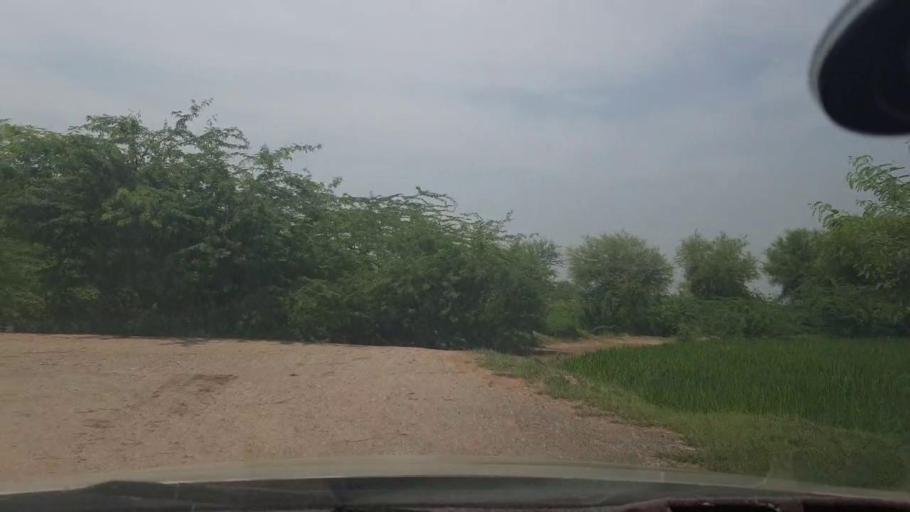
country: PK
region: Sindh
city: Jacobabad
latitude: 28.2412
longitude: 68.4195
